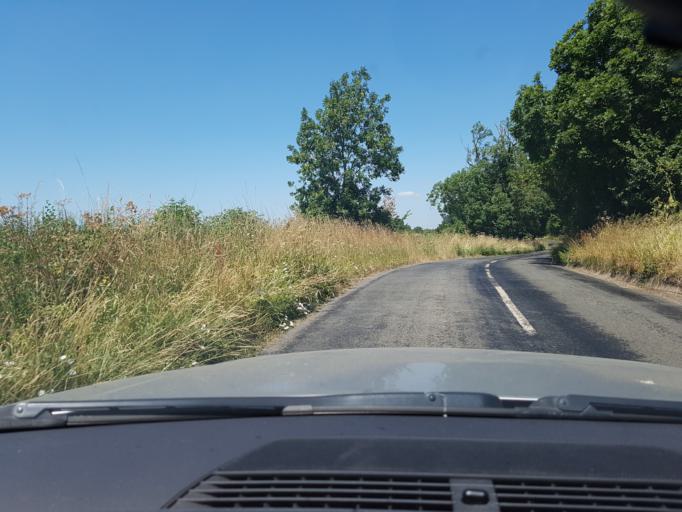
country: GB
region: England
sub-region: Milton Keynes
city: Calverton
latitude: 52.0368
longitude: -0.8415
